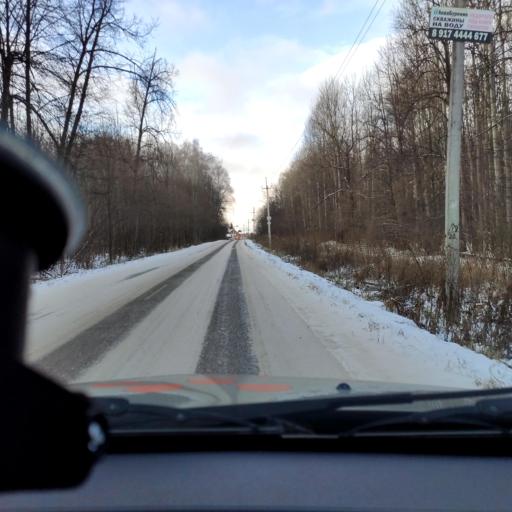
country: RU
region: Bashkortostan
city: Avdon
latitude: 54.7827
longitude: 55.7409
